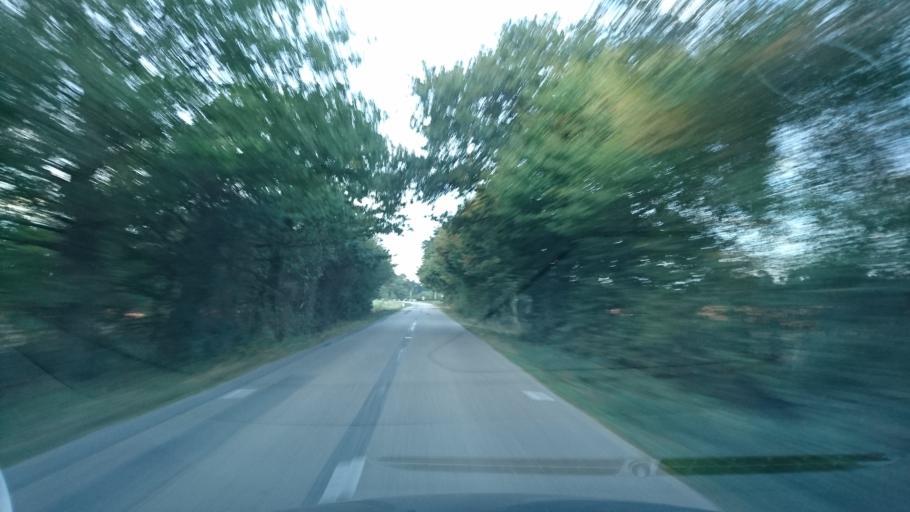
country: FR
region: Brittany
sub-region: Departement d'Ille-et-Vilaine
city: Saint-Just
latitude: 47.8030
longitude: -2.0095
